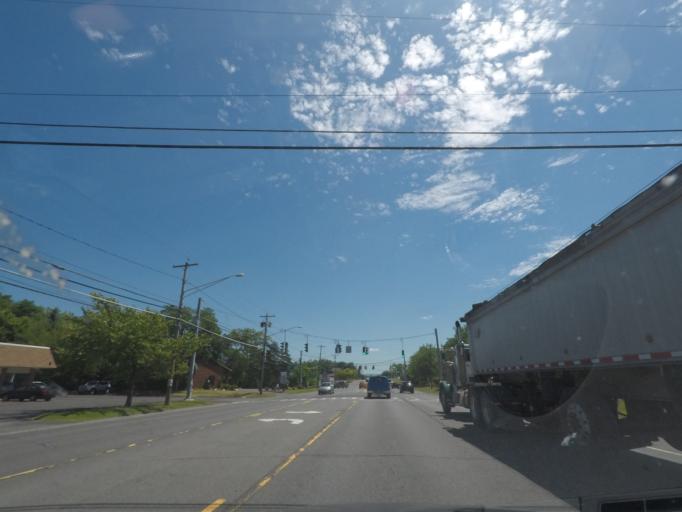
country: US
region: New York
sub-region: Albany County
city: Watervliet
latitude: 42.7452
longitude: -73.7536
